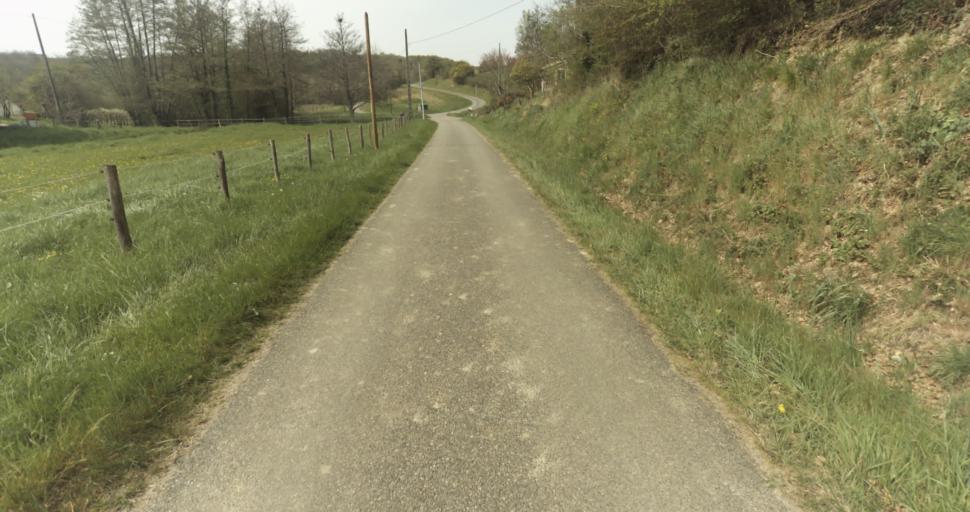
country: FR
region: Midi-Pyrenees
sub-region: Departement du Tarn-et-Garonne
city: Moissac
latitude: 44.1063
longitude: 1.0575
